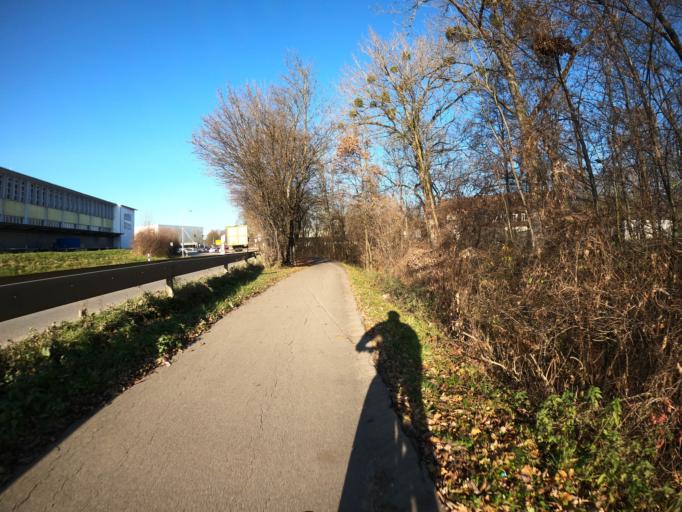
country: DE
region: Baden-Wuerttemberg
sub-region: Regierungsbezirk Stuttgart
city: Goeppingen
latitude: 48.6890
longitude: 9.6713
